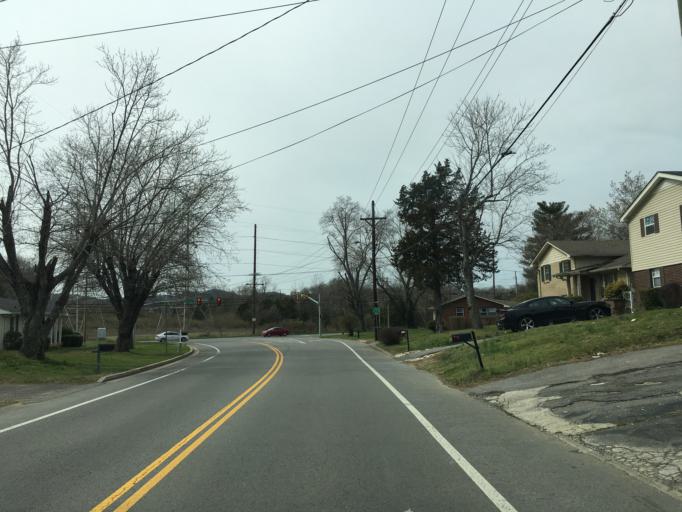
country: US
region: Tennessee
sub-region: Williamson County
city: Brentwood
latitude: 36.0519
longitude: -86.7420
